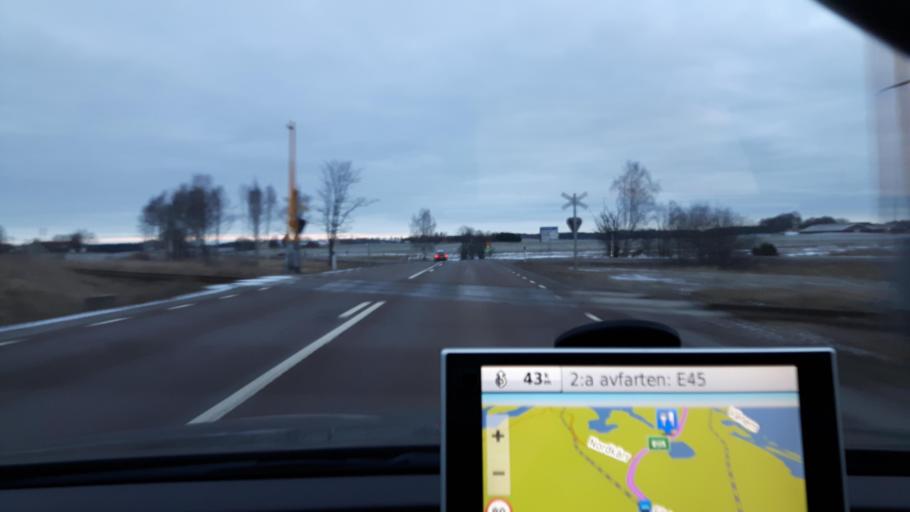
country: SE
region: Vaestra Goetaland
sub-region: Melleruds Kommun
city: Mellerud
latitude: 58.7191
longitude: 12.4557
